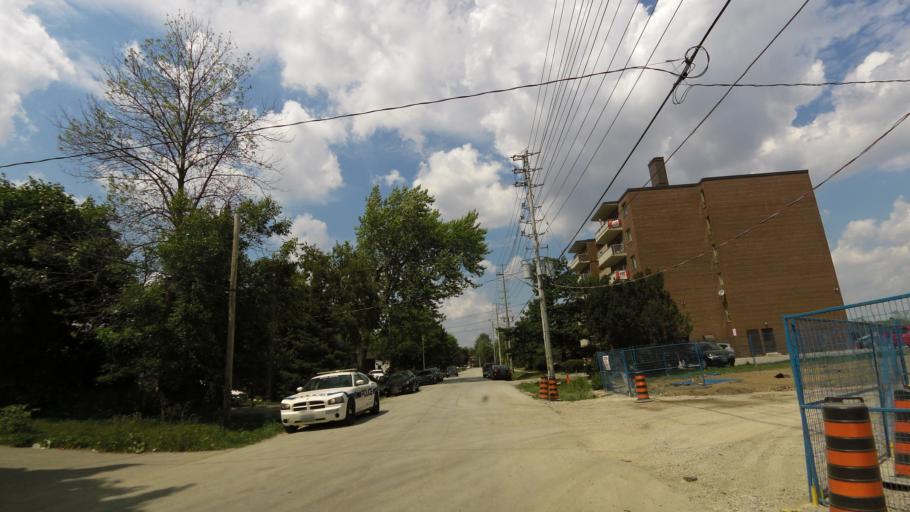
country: CA
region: Ontario
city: Mississauga
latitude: 43.5654
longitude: -79.5721
